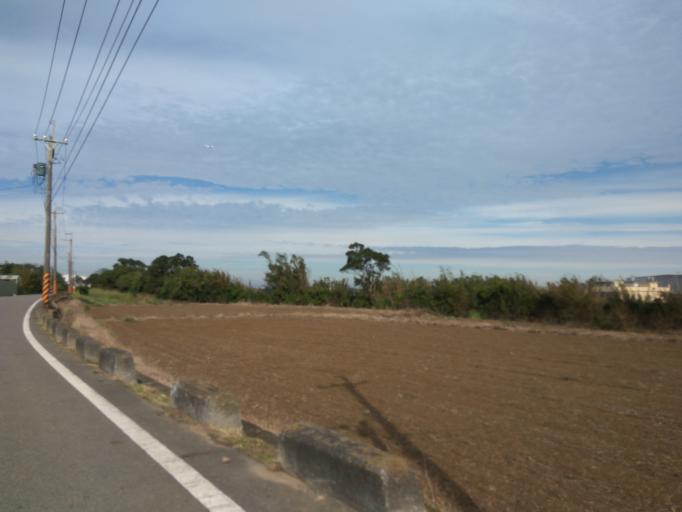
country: TW
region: Taiwan
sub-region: Hsinchu
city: Zhubei
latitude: 24.9577
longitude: 121.1088
